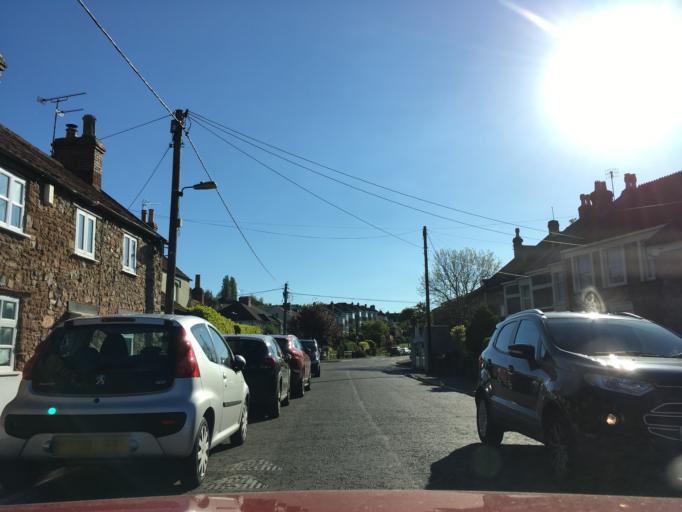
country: GB
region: England
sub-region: North Somerset
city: Long Ashton
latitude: 51.4287
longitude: -2.6674
